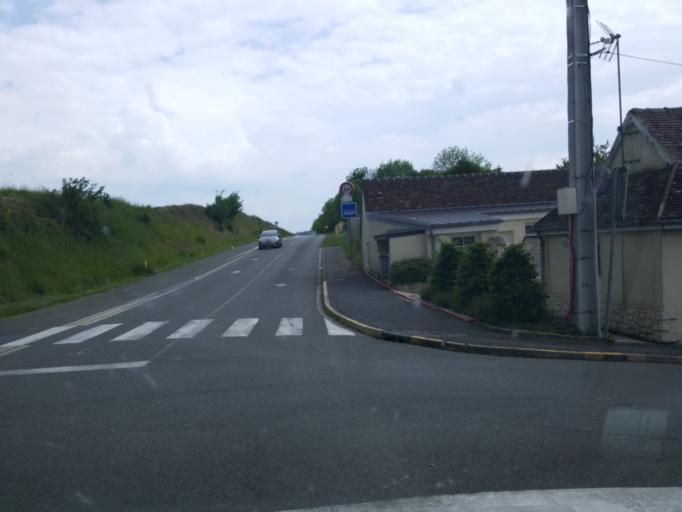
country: FR
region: Picardie
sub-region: Departement de l'Oise
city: Allonne
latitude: 49.4252
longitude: 2.1346
